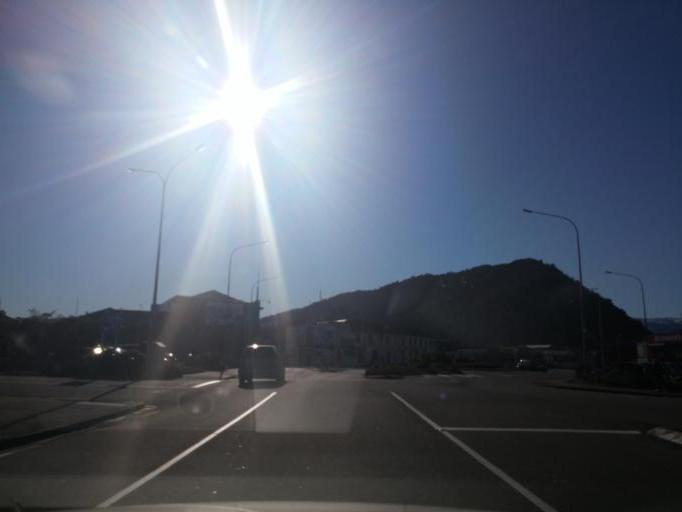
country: NZ
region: West Coast
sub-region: Grey District
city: Greymouth
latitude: -42.4506
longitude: 171.2106
